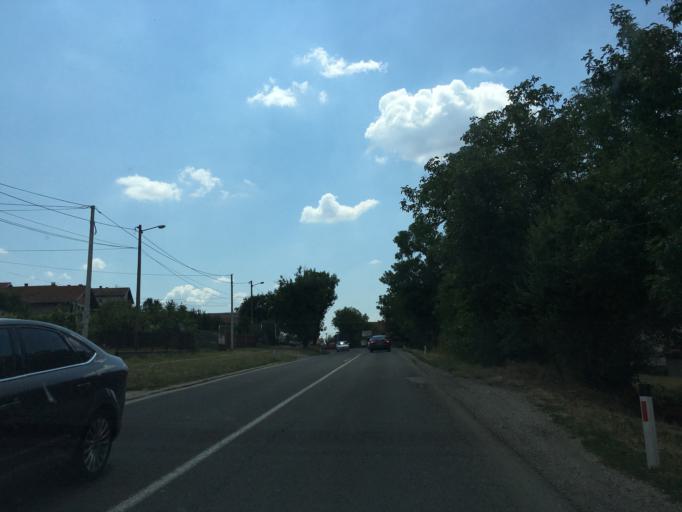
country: RS
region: Central Serbia
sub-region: Belgrade
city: Mladenovac
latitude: 44.4567
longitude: 20.6763
